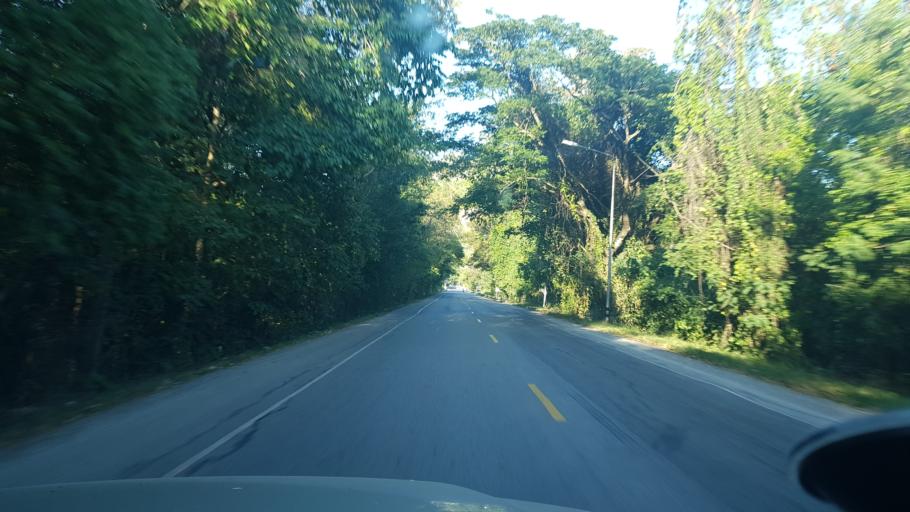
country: TH
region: Khon Kaen
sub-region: Amphoe Phu Pha Man
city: Phu Pha Man
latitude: 16.6498
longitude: 101.8091
